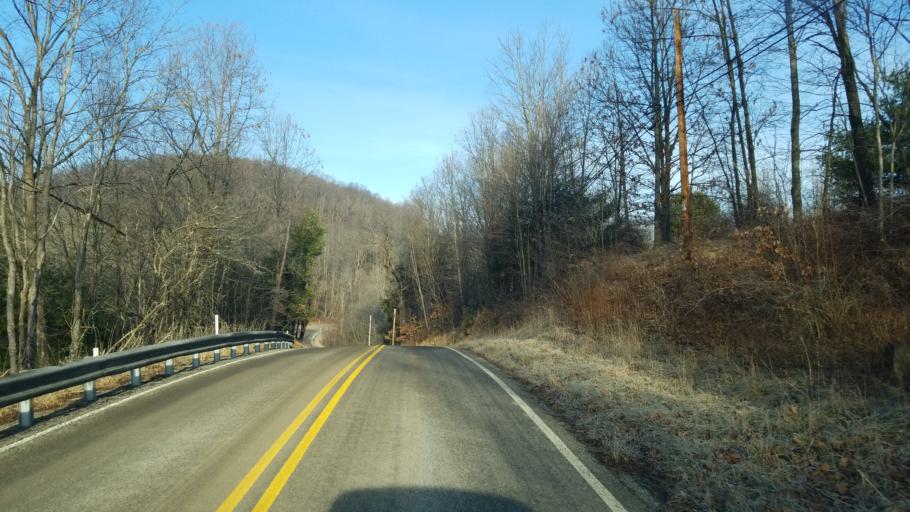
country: US
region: Pennsylvania
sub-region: Jefferson County
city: Brookville
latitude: 40.9622
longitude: -79.2508
